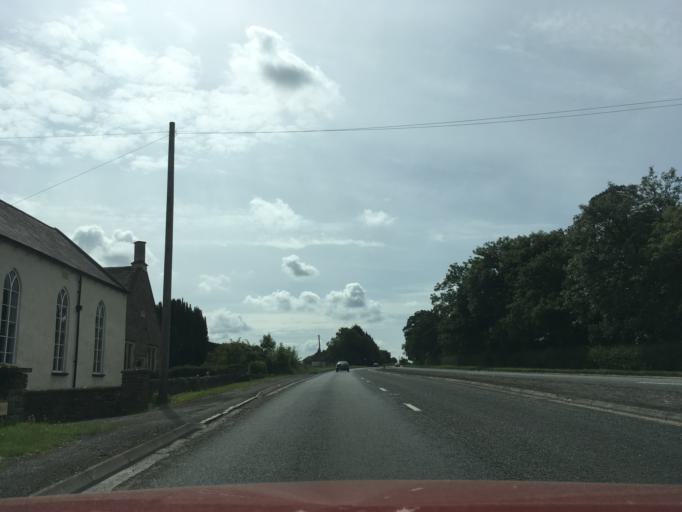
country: GB
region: England
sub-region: South Gloucestershire
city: Falfield
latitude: 51.6317
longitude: -2.4614
